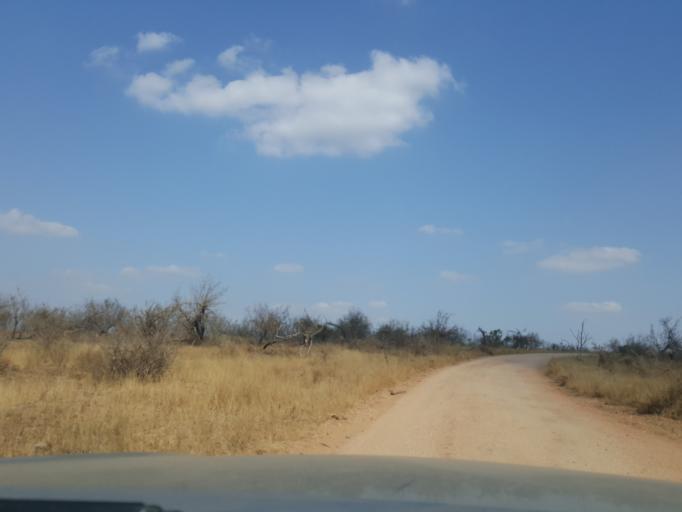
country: ZA
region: Mpumalanga
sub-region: Ehlanzeni District
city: Komatipoort
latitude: -25.2988
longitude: 31.7581
